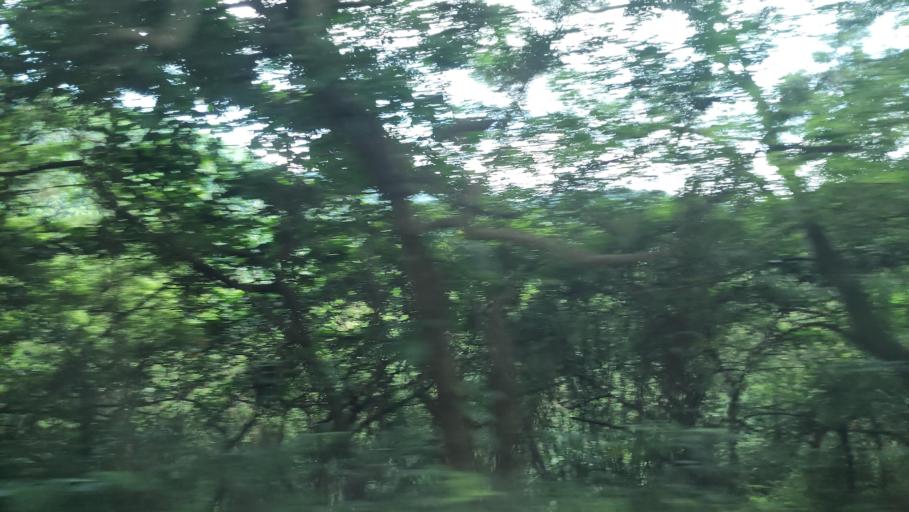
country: TW
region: Taipei
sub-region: Taipei
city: Banqiao
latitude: 24.8880
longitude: 121.4243
